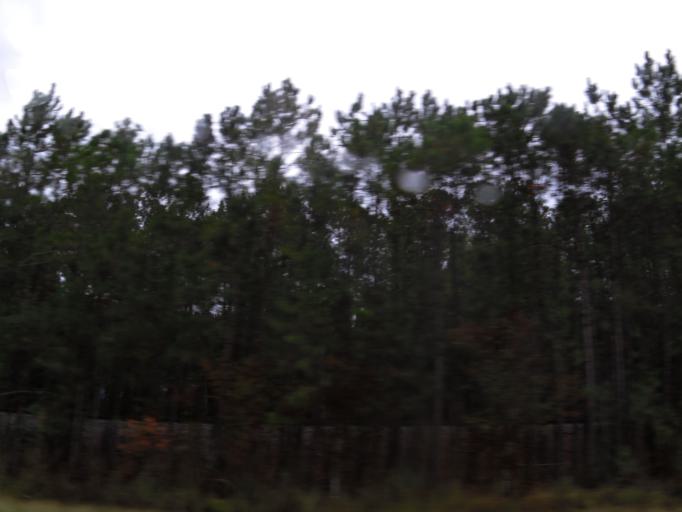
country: US
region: Georgia
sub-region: Wayne County
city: Jesup
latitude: 31.5512
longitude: -81.8134
